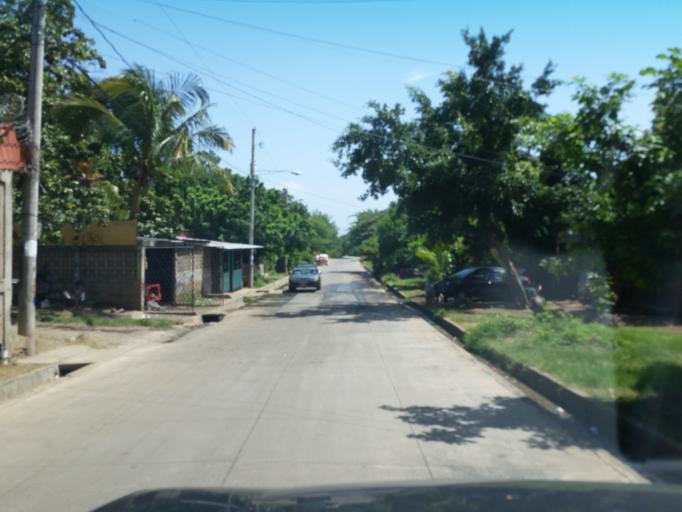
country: NI
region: Managua
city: Managua
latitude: 12.1010
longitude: -86.2251
